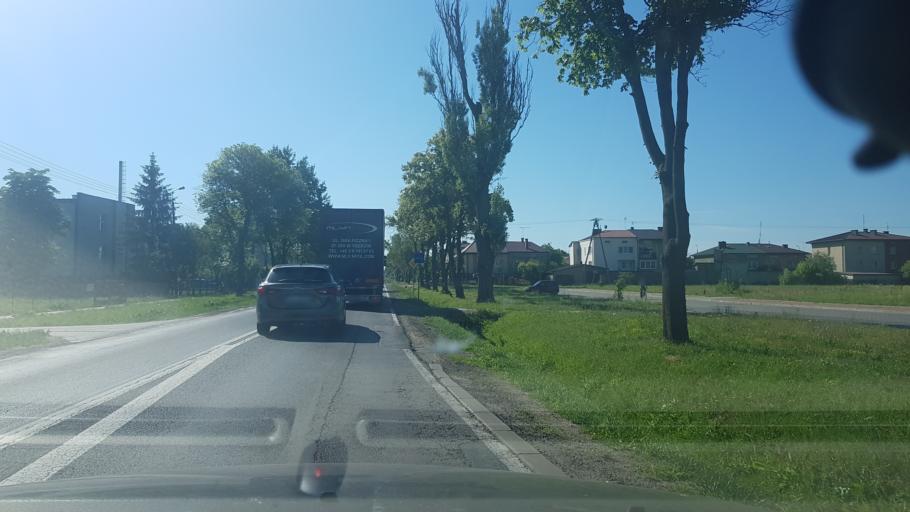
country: PL
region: Masovian Voivodeship
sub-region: Powiat wegrowski
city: Lochow
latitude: 52.5289
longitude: 21.6840
